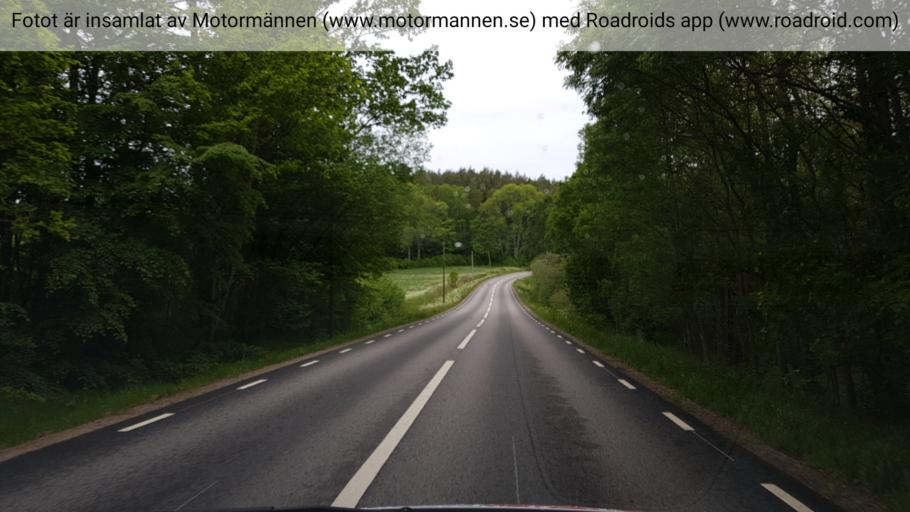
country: SE
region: Kalmar
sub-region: Vasterviks Kommun
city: Vaestervik
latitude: 57.9159
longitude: 16.6285
